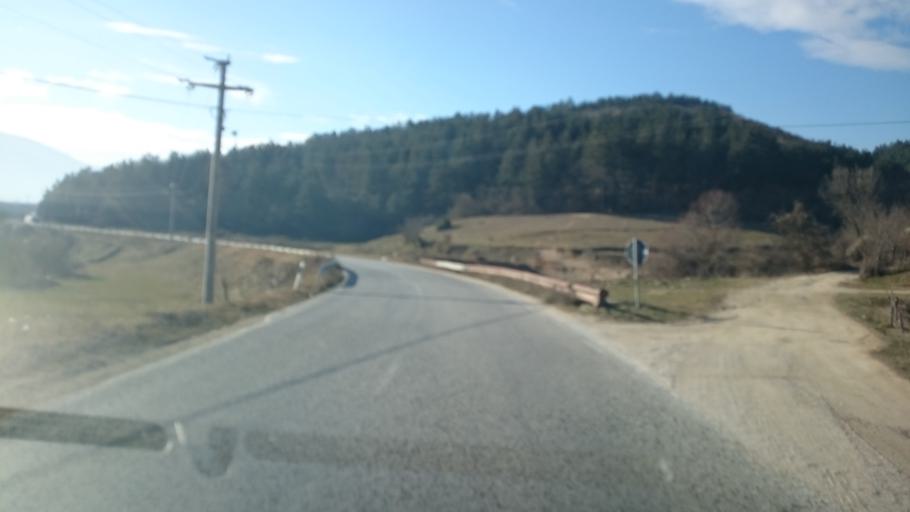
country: MK
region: Plasnica
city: Plasnica
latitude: 41.4840
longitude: 21.1086
